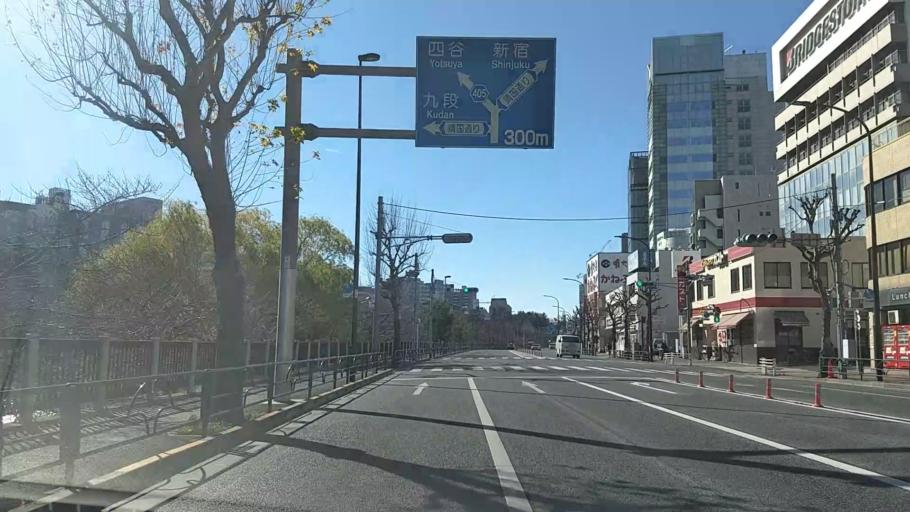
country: JP
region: Tokyo
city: Tokyo
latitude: 35.6950
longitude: 139.7383
